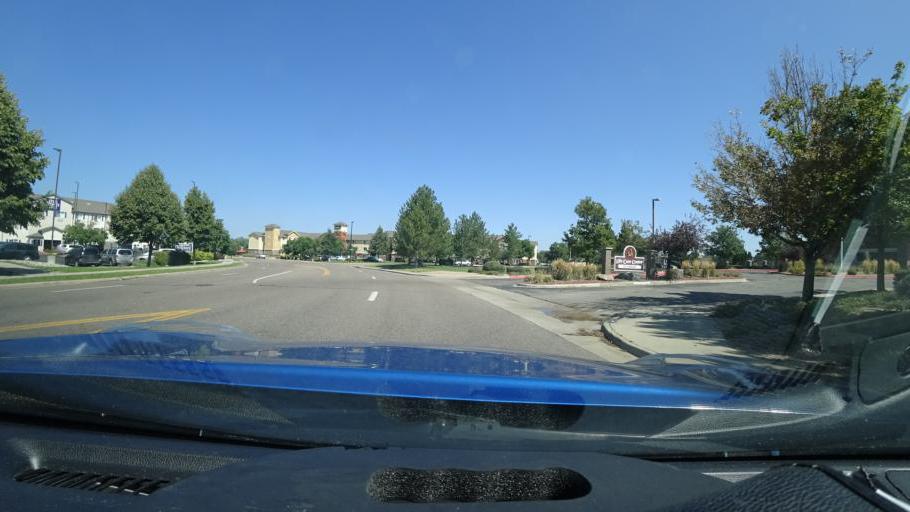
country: US
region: Colorado
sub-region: Adams County
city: Aurora
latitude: 39.6784
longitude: -104.8240
